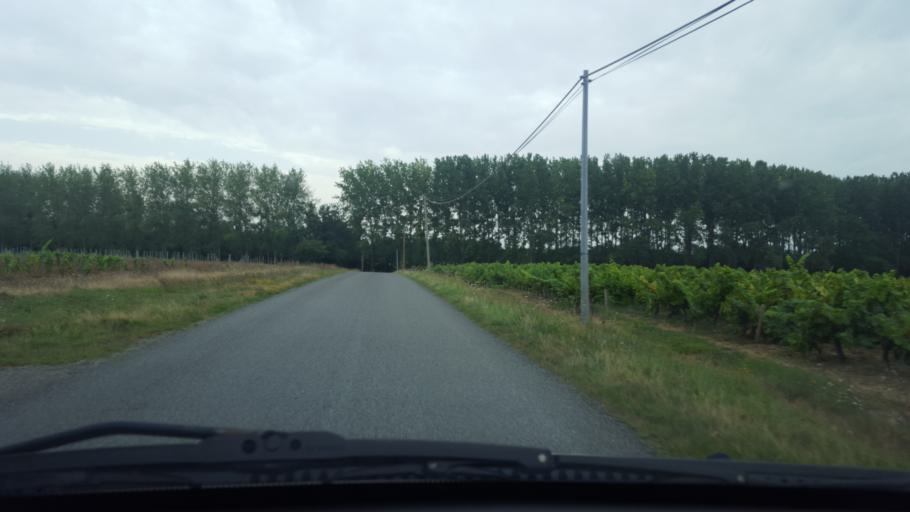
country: FR
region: Pays de la Loire
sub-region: Departement de la Loire-Atlantique
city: Saint-Philbert-de-Grand-Lieu
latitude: 47.0154
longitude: -1.6348
